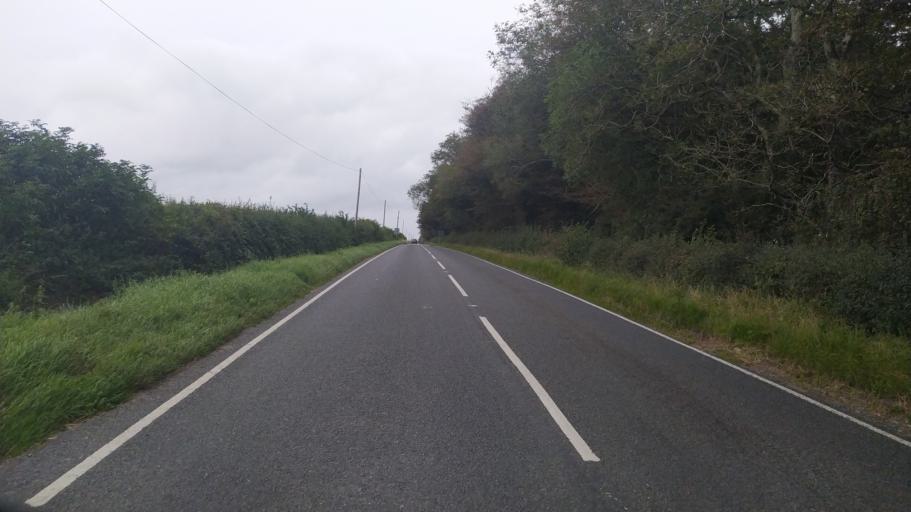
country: GB
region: England
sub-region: Dorset
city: Dorchester
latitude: 50.8021
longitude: -2.4531
